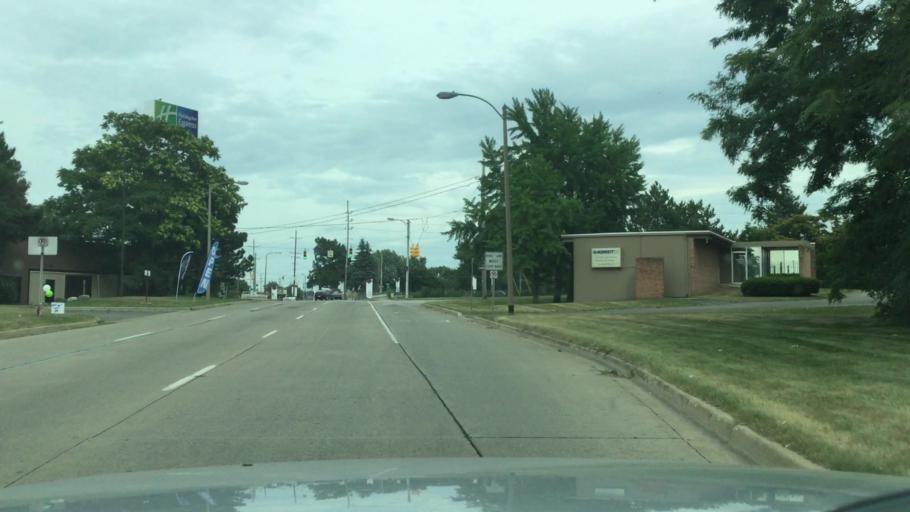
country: US
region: Michigan
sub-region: Genesee County
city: Flint
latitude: 43.0247
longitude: -83.6833
